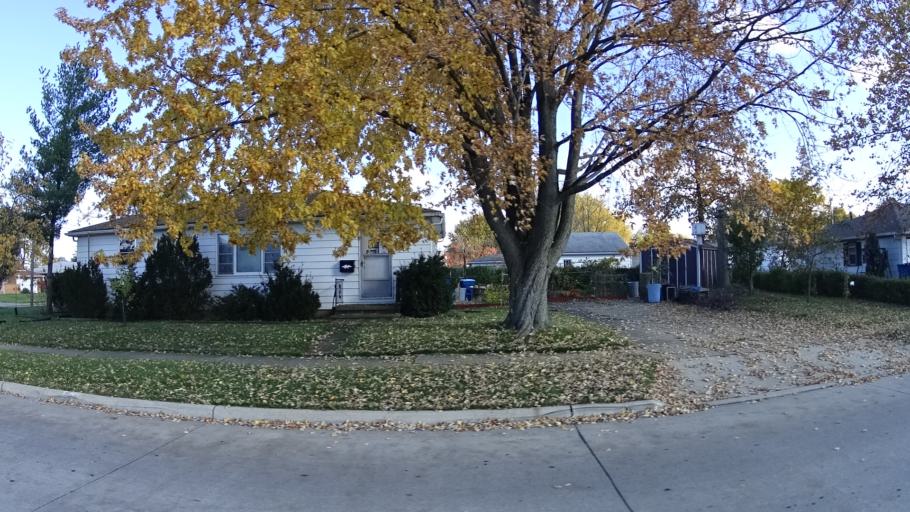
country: US
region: Ohio
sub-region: Lorain County
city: Lorain
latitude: 41.4463
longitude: -82.1888
